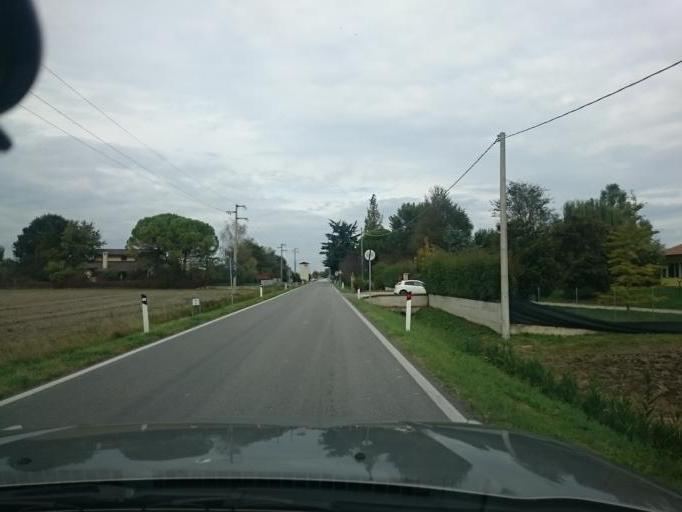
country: IT
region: Veneto
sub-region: Provincia di Padova
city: Codevigo
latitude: 45.2423
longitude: 12.0981
